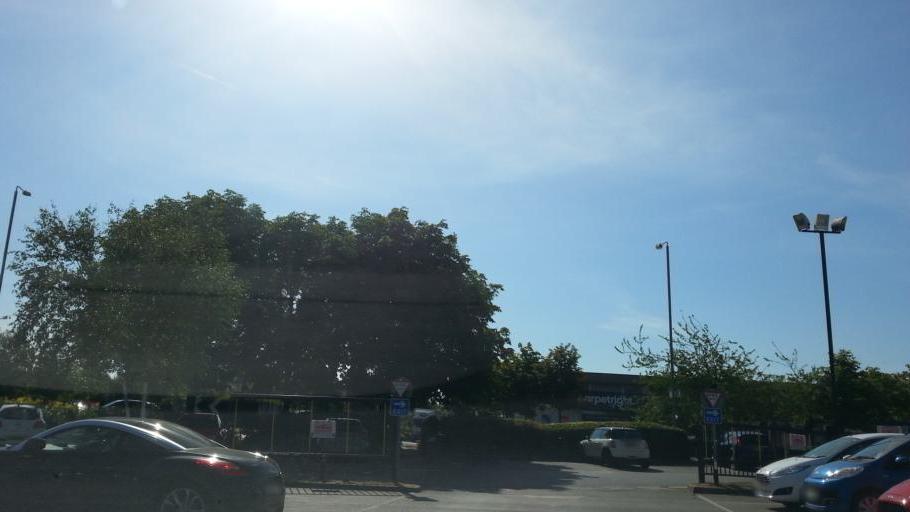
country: GB
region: England
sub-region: Derbyshire
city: Long Eaton
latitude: 52.9035
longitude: -1.2442
